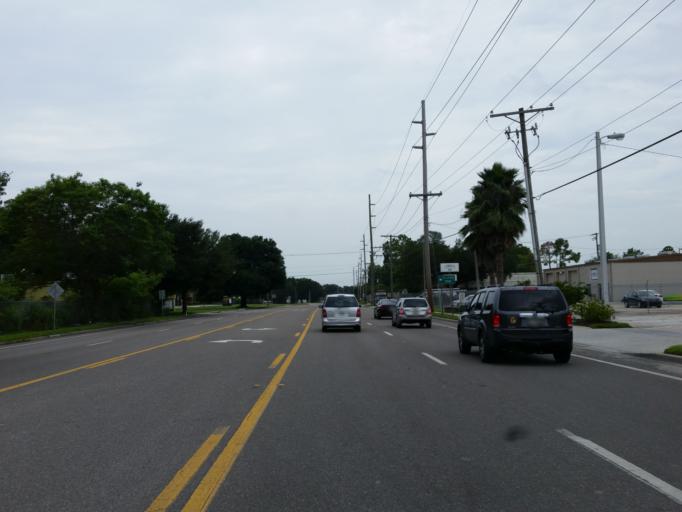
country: US
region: Florida
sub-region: Hillsborough County
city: Mango
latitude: 27.9496
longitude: -82.3350
